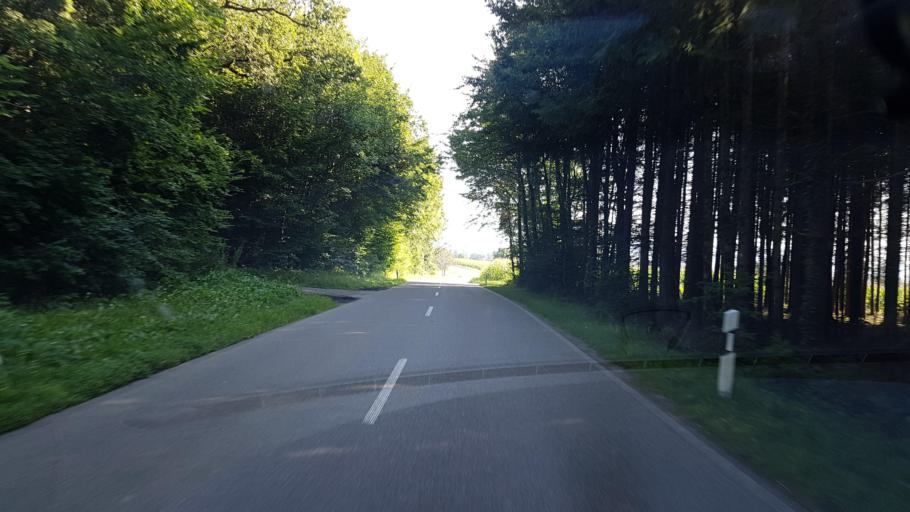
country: DE
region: Baden-Wuerttemberg
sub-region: Freiburg Region
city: Albbruck
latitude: 47.6078
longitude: 8.1120
